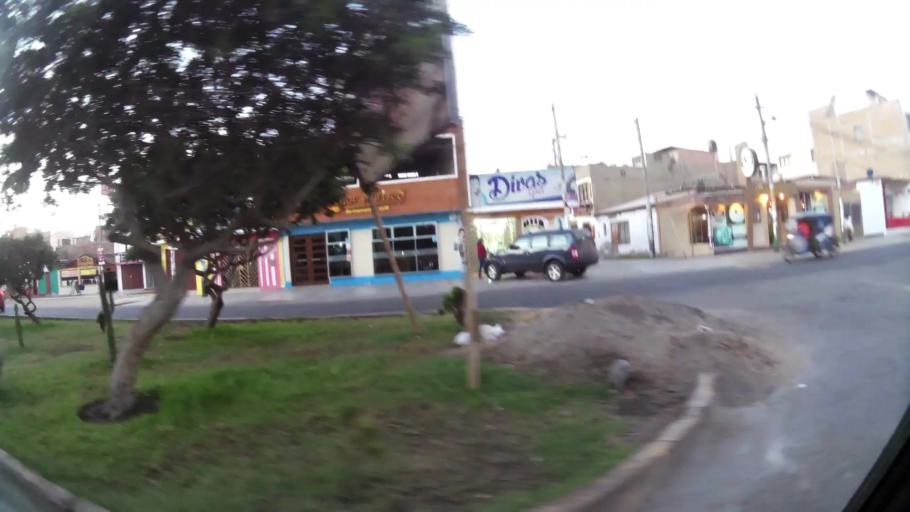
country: PE
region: Ancash
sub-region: Provincia de Santa
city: Buenos Aires
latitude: -9.1224
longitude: -78.5290
